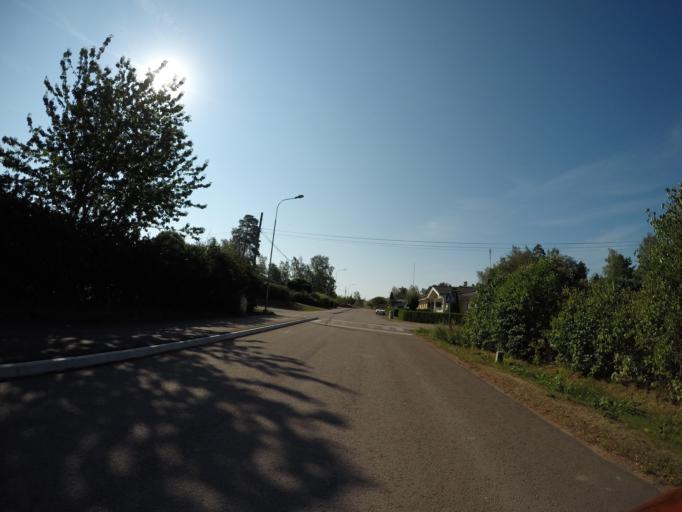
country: AX
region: Alands landsbygd
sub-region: Finstroem
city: Finstroem
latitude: 60.2282
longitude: 19.9785
